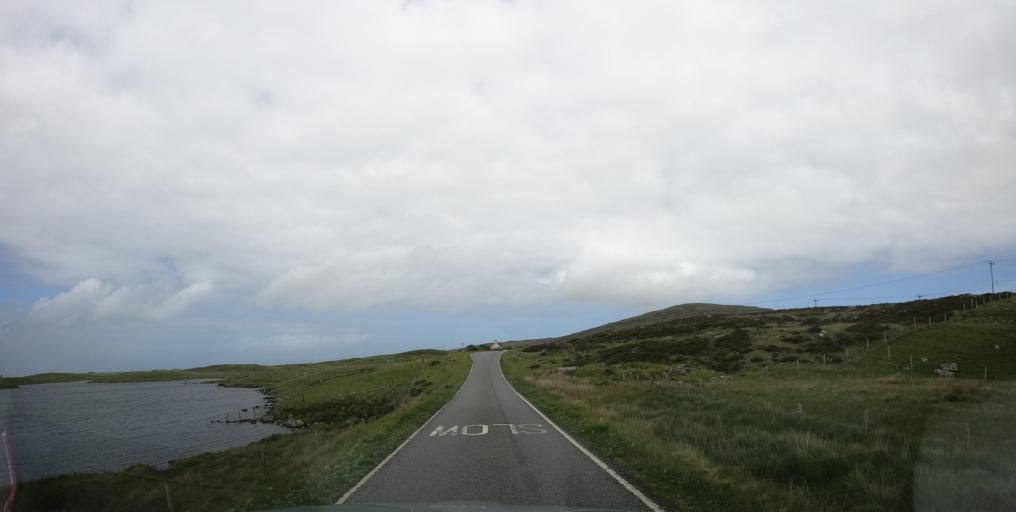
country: GB
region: Scotland
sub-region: Eilean Siar
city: Isle of South Uist
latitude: 57.2923
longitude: -7.3655
